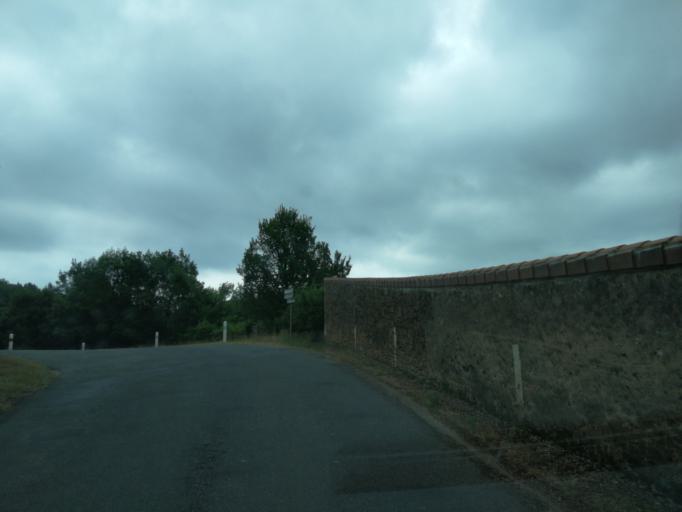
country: FR
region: Aquitaine
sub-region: Departement du Lot-et-Garonne
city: Montayral
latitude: 44.5401
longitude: 1.0775
